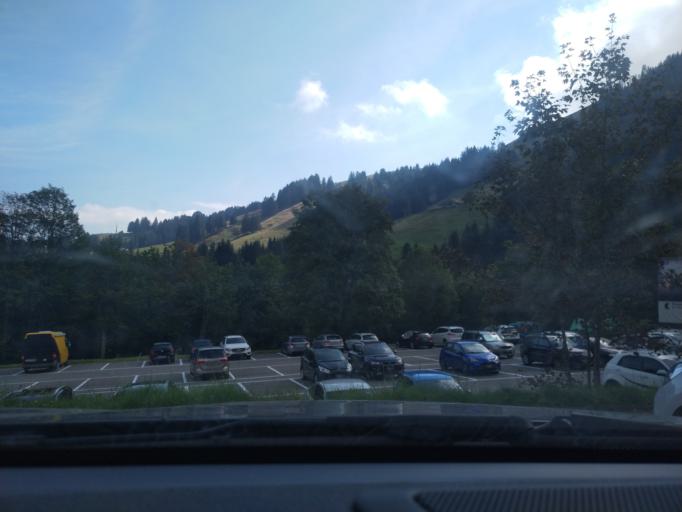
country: CH
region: Fribourg
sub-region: Gruyere District
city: Gruyeres
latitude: 46.5605
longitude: 7.0383
